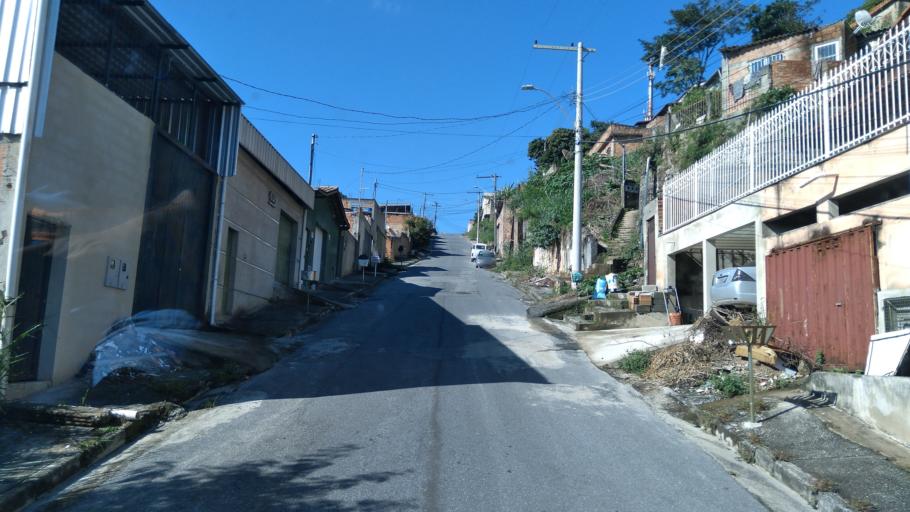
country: BR
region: Minas Gerais
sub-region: Santa Luzia
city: Santa Luzia
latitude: -19.8285
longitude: -43.8970
